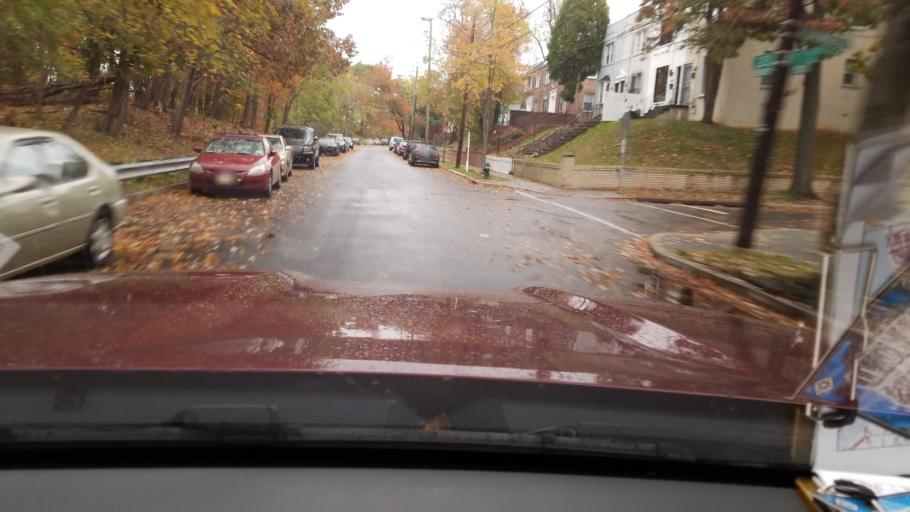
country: US
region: Maryland
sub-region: Prince George's County
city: Glassmanor
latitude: 38.8477
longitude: -77.0055
